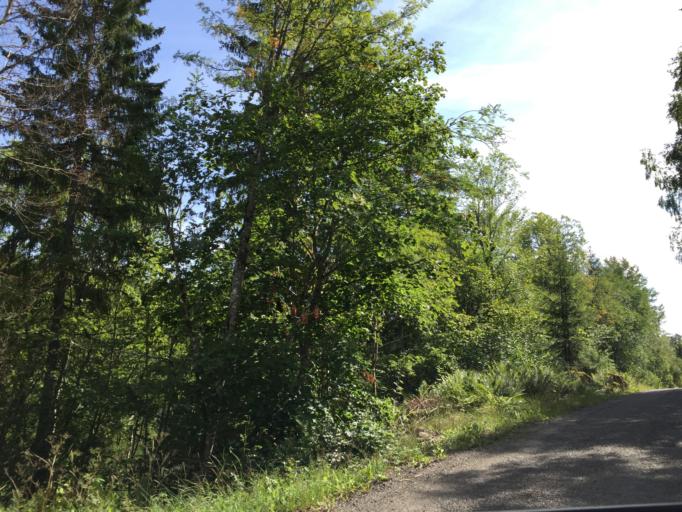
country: NO
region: Vestfold
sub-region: Hof
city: Hof
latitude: 59.4450
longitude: 10.1570
